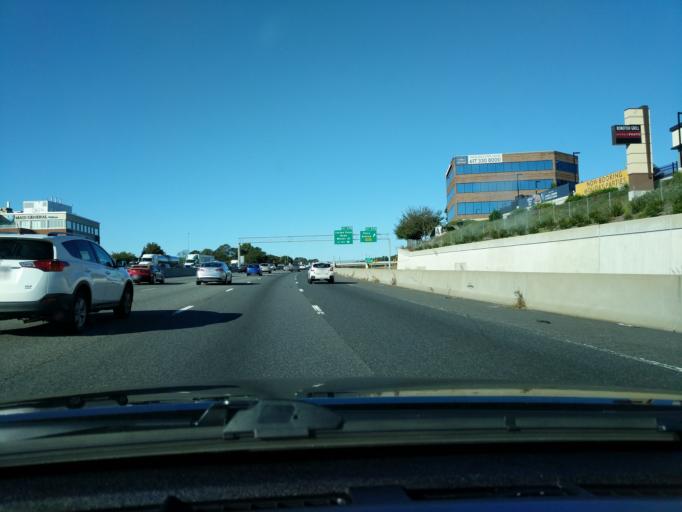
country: US
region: Massachusetts
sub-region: Middlesex County
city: Waltham
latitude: 42.3937
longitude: -71.2623
